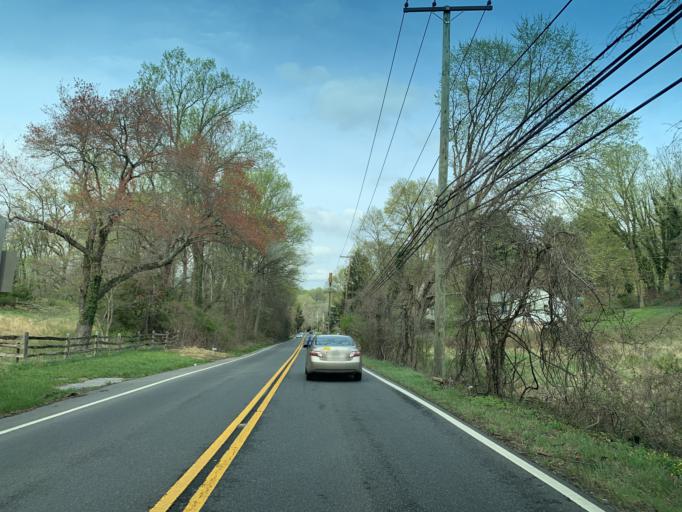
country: US
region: Maryland
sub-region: Montgomery County
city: Leisure World
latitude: 39.1161
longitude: -77.0508
